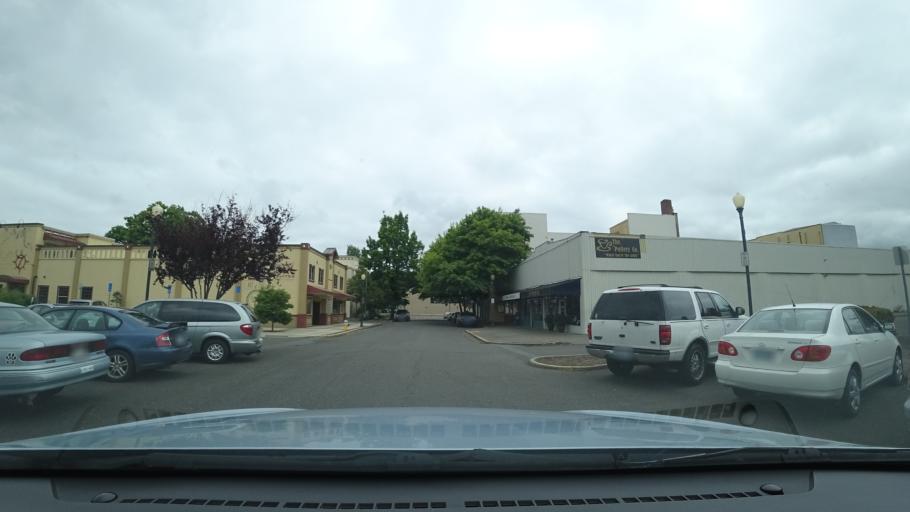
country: US
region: Oregon
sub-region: Coos County
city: Coos Bay
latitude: 43.3662
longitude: -124.2147
